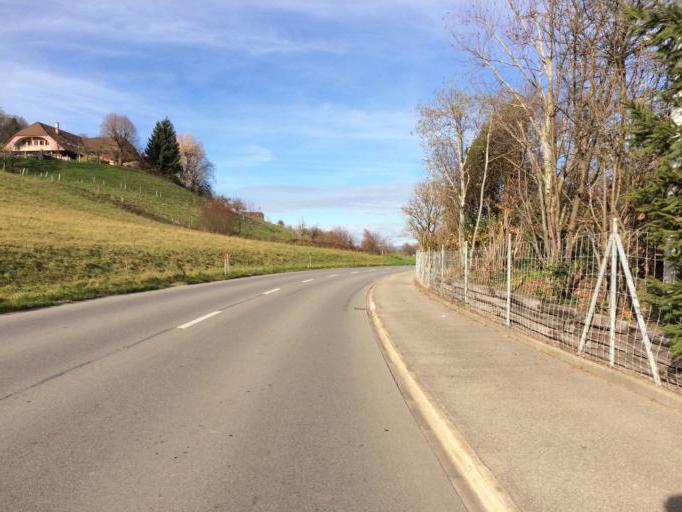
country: CH
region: Bern
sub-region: Bern-Mittelland District
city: Belp
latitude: 46.8993
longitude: 7.4872
